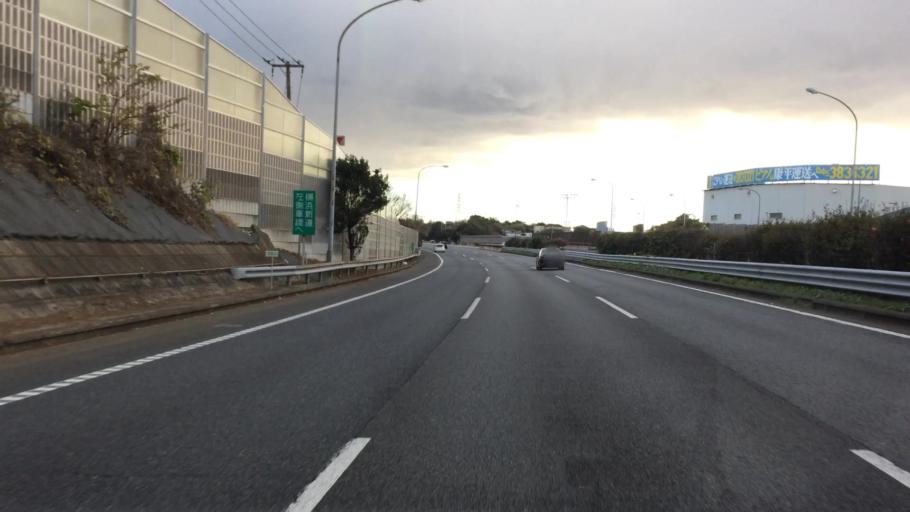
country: JP
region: Kanagawa
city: Yokohama
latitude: 35.4885
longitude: 139.5923
